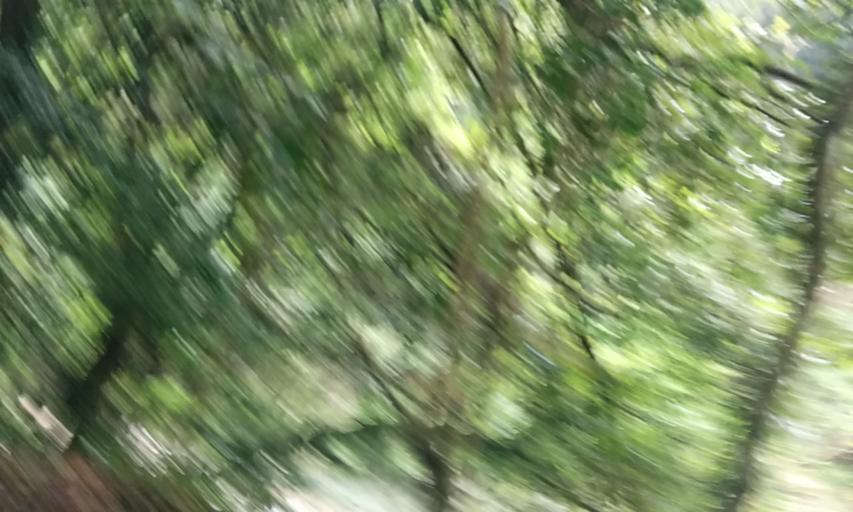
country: JP
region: Kyoto
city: Kameoka
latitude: 35.0477
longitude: 135.6613
